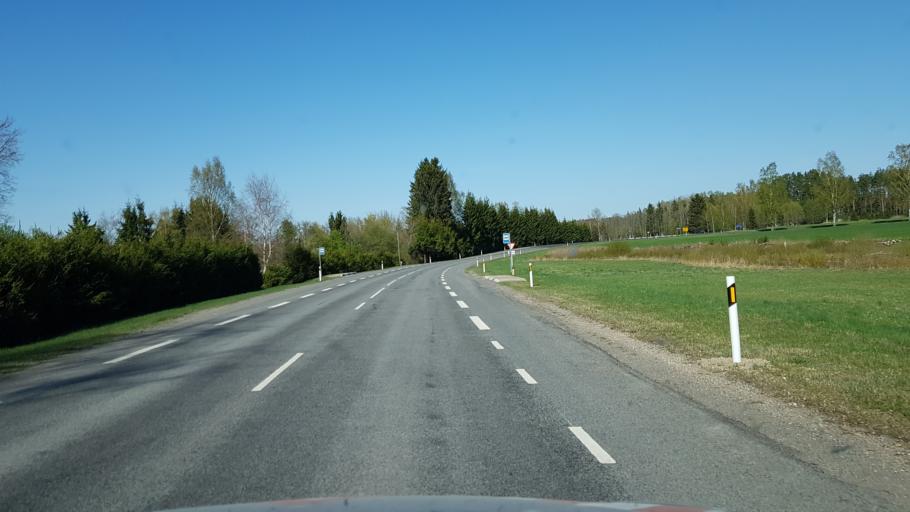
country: EE
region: Viljandimaa
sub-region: Viljandi linn
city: Viljandi
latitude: 58.3204
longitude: 25.5704
